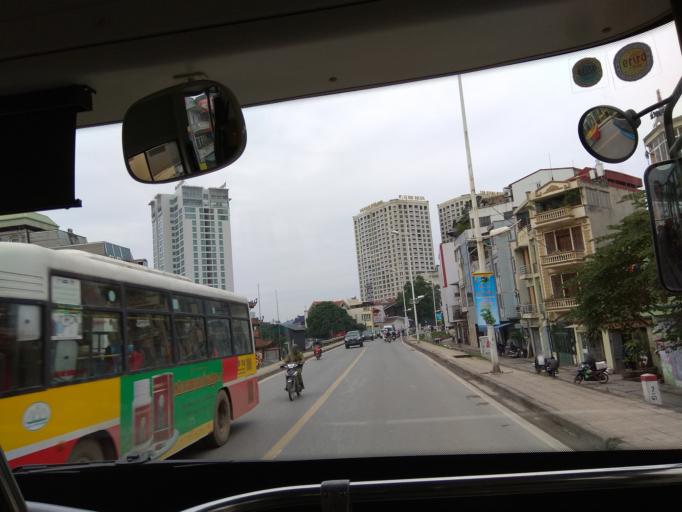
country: VN
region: Ha Noi
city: Tay Ho
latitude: 21.0648
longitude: 105.8304
